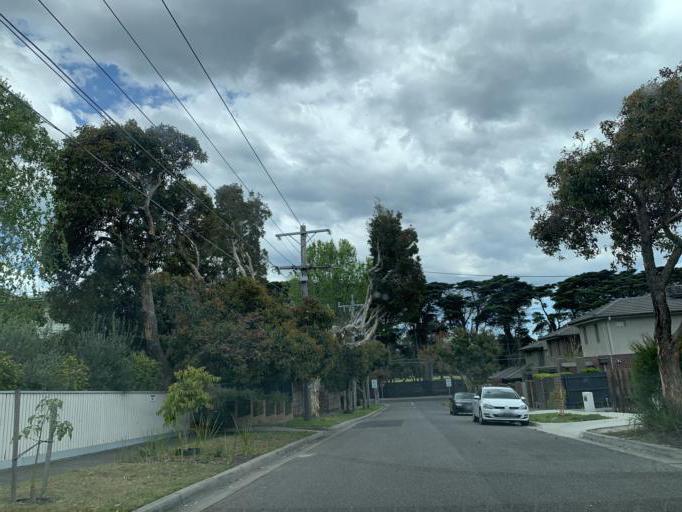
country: AU
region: Victoria
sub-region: Bayside
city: Cheltenham
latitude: -37.9632
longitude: 145.0450
